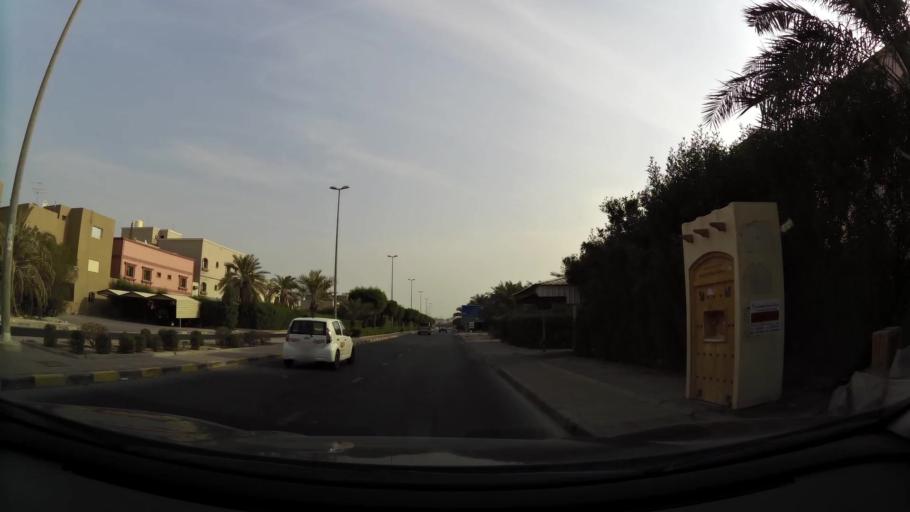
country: KW
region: Mubarak al Kabir
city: Sabah as Salim
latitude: 29.2244
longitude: 48.0603
